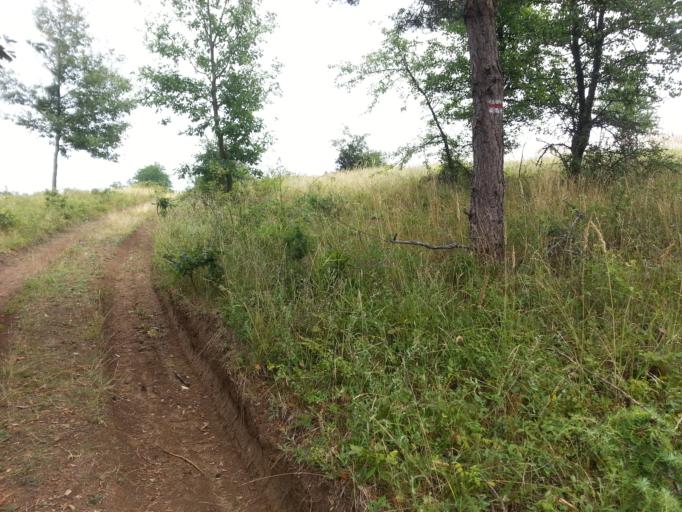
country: HU
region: Heves
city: Sirok
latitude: 47.9756
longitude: 20.2006
